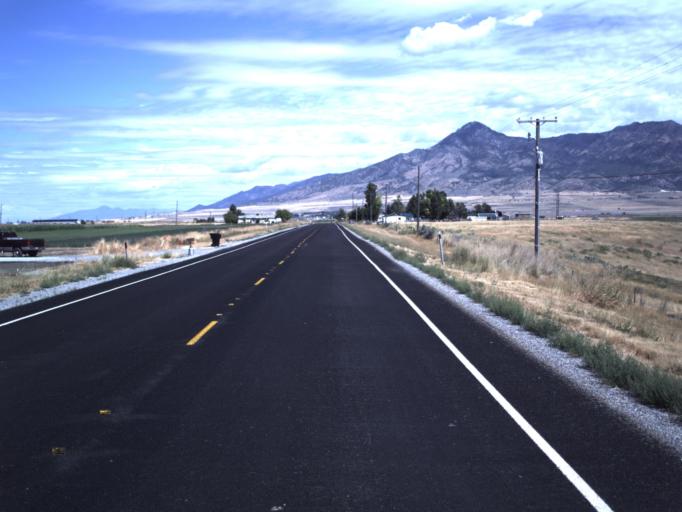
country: US
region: Utah
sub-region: Box Elder County
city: Garland
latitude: 41.8238
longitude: -112.1455
